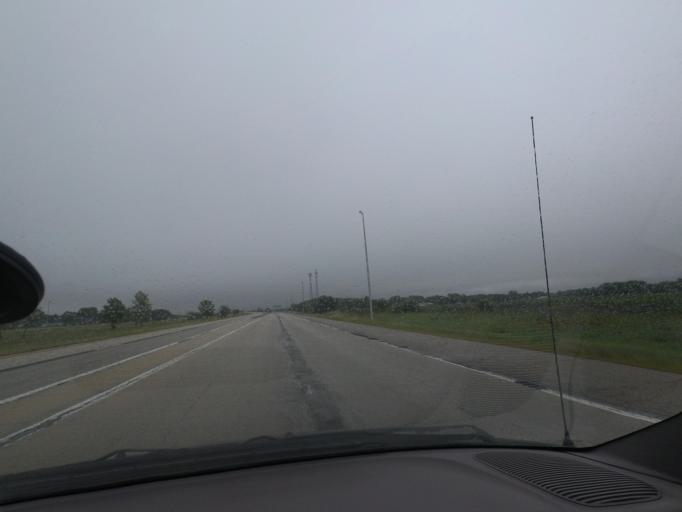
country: US
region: Illinois
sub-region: Macon County
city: Harristown
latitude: 39.8358
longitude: -89.0582
